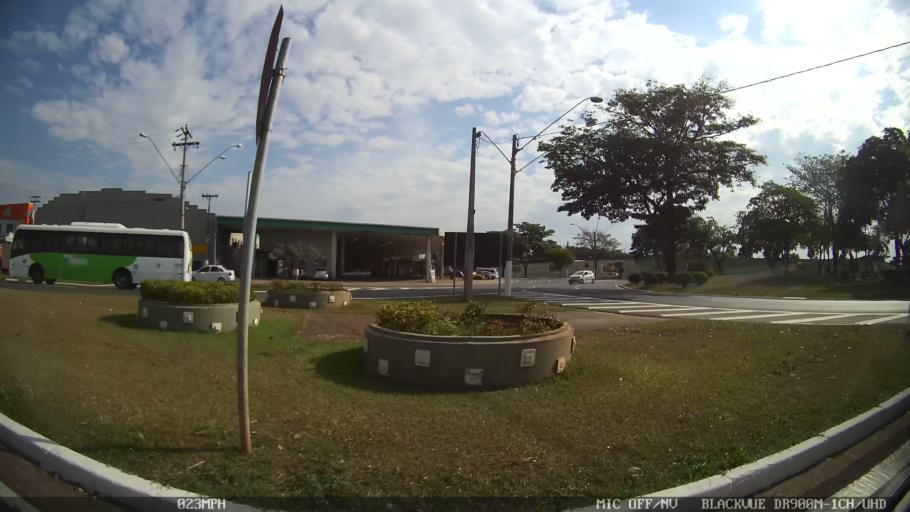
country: BR
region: Sao Paulo
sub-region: Paulinia
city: Paulinia
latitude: -22.7710
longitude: -47.1470
